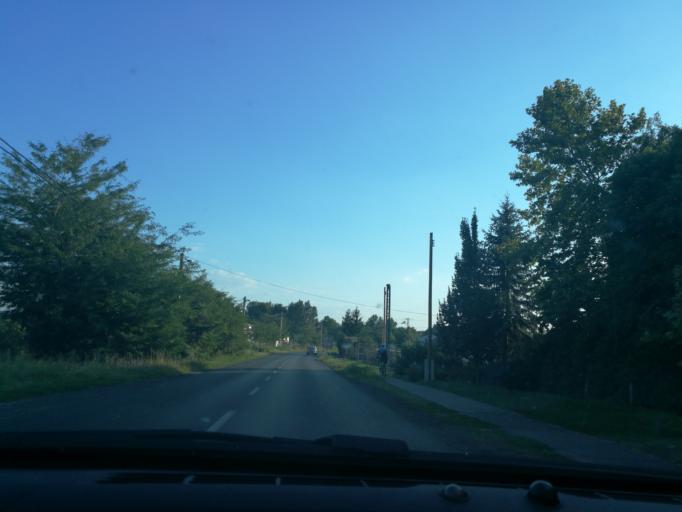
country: HU
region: Szabolcs-Szatmar-Bereg
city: Kotaj
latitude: 48.0213
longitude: 21.7435
